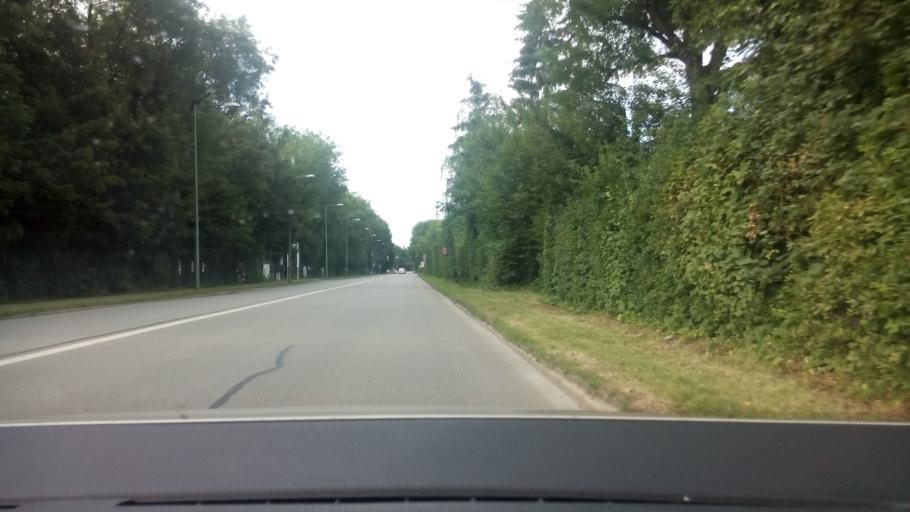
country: DE
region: Bavaria
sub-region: Upper Bavaria
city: Unterfoehring
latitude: 48.1977
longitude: 11.6255
